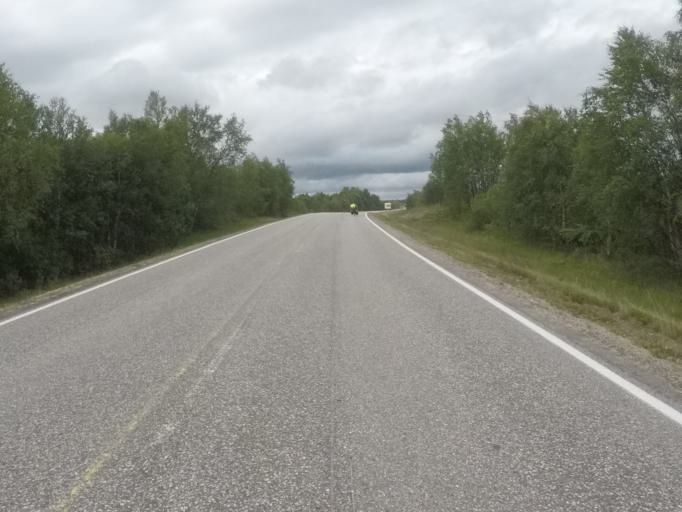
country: FI
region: Lapland
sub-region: Tunturi-Lappi
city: Enontekioe
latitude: 68.4832
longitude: 23.3607
